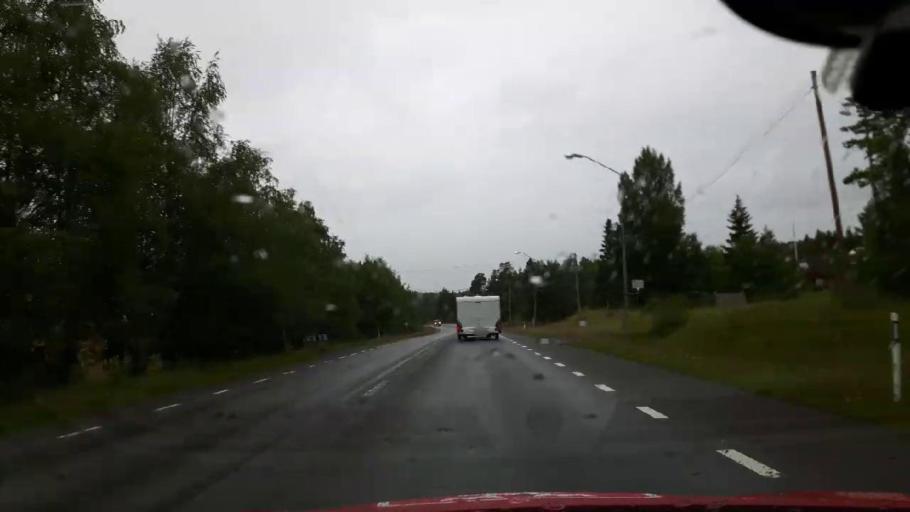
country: SE
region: Jaemtland
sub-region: Are Kommun
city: Jarpen
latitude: 63.3339
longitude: 13.5195
